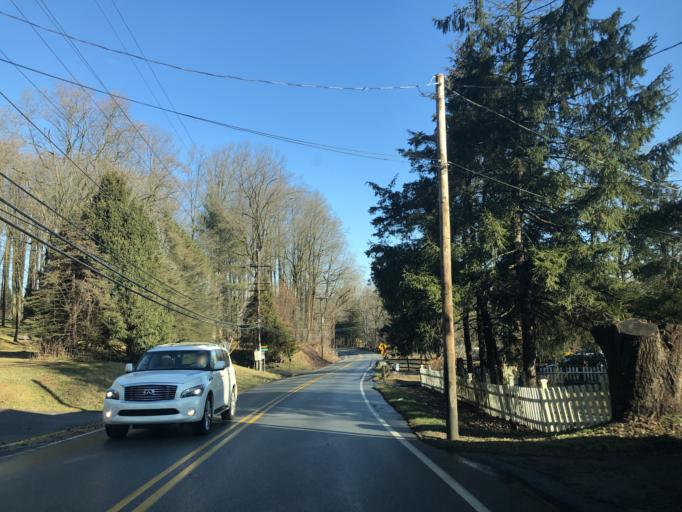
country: US
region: Pennsylvania
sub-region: Delaware County
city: Chester Heights
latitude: 39.9124
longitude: -75.4841
